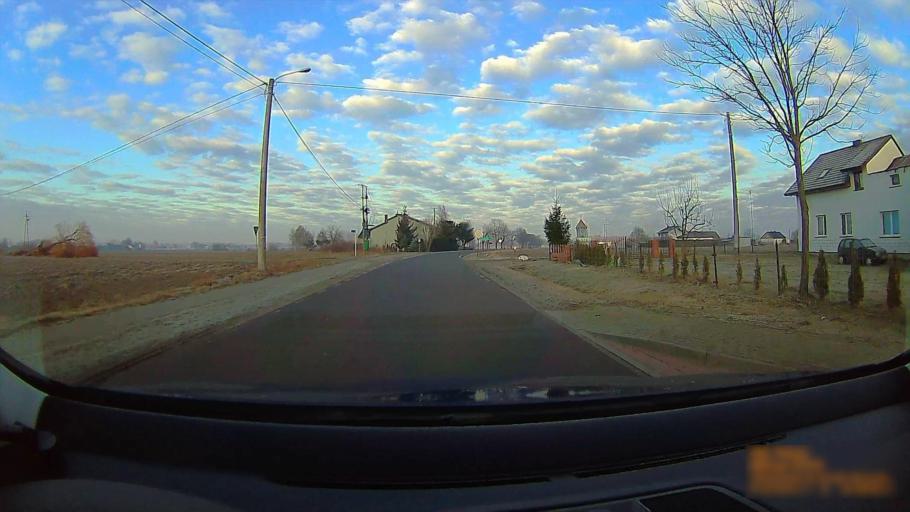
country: PL
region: Greater Poland Voivodeship
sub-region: Powiat koninski
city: Rychwal
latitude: 52.0977
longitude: 18.1130
